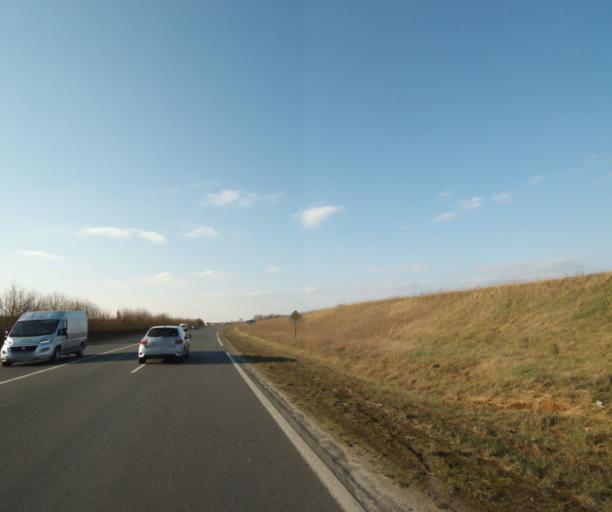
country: FR
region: Poitou-Charentes
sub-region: Departement des Deux-Sevres
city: Vouille
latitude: 46.3117
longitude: -0.3799
